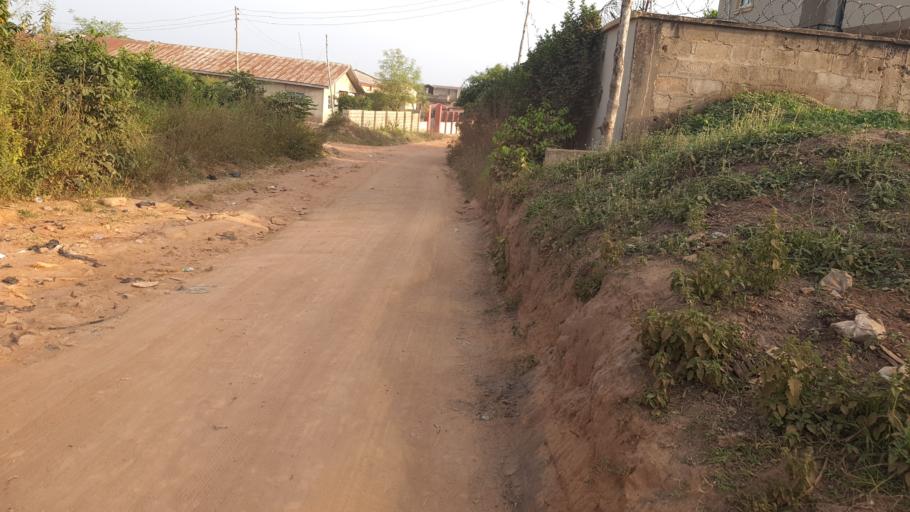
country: NG
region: Osun
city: Iwo
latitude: 7.6248
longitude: 4.1580
